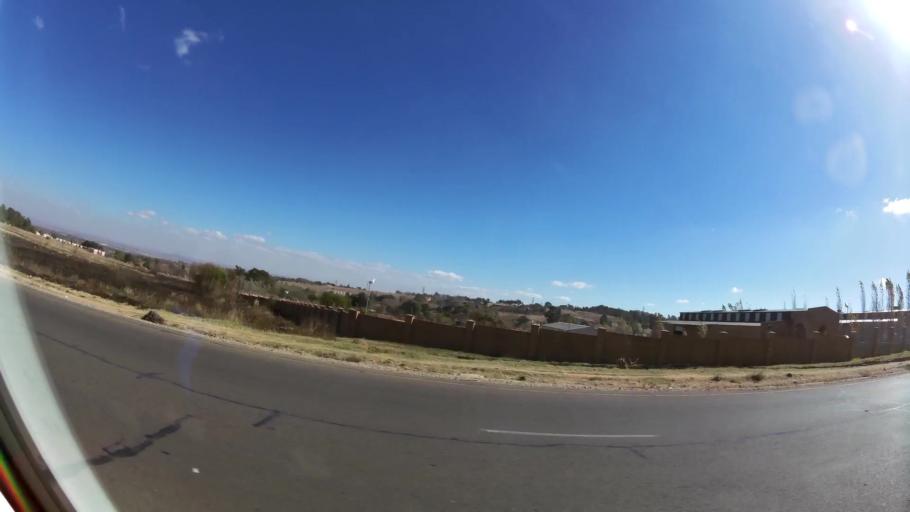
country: ZA
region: Gauteng
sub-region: City of Johannesburg Metropolitan Municipality
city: Midrand
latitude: -25.9474
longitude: 28.0909
